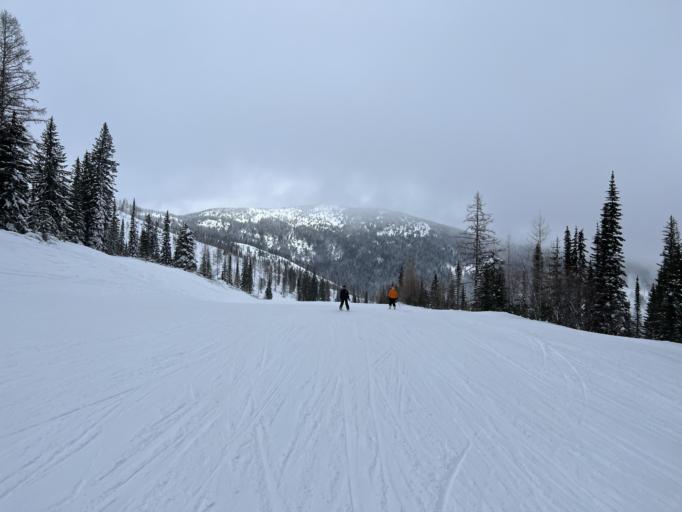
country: US
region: Idaho
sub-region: Bonner County
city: Ponderay
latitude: 48.3825
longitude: -116.6189
